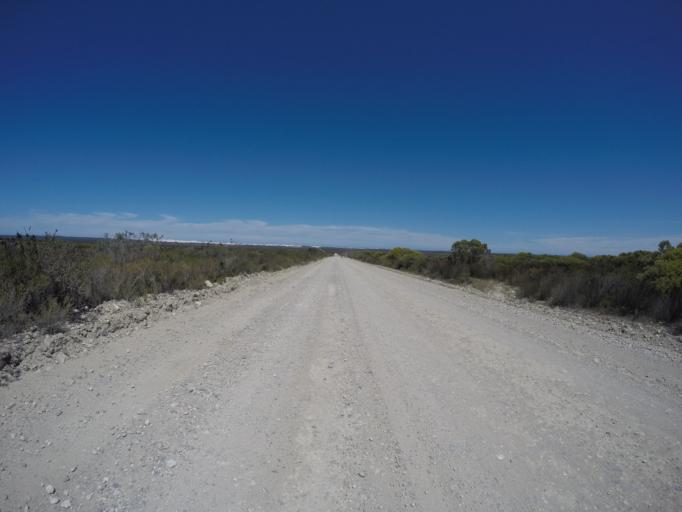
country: ZA
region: Western Cape
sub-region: Overberg District Municipality
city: Bredasdorp
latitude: -34.4382
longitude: 20.4206
